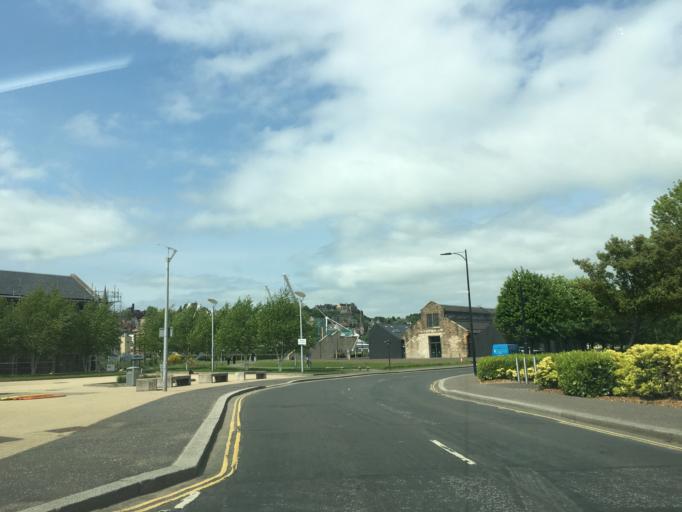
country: GB
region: Scotland
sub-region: Stirling
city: Stirling
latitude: 56.1187
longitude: -3.9306
